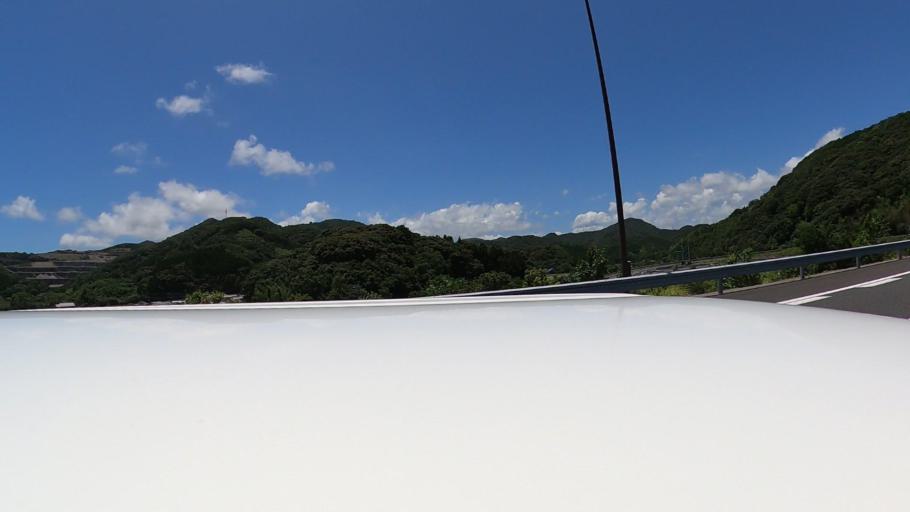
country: JP
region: Miyazaki
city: Nobeoka
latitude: 32.3999
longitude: 131.6171
